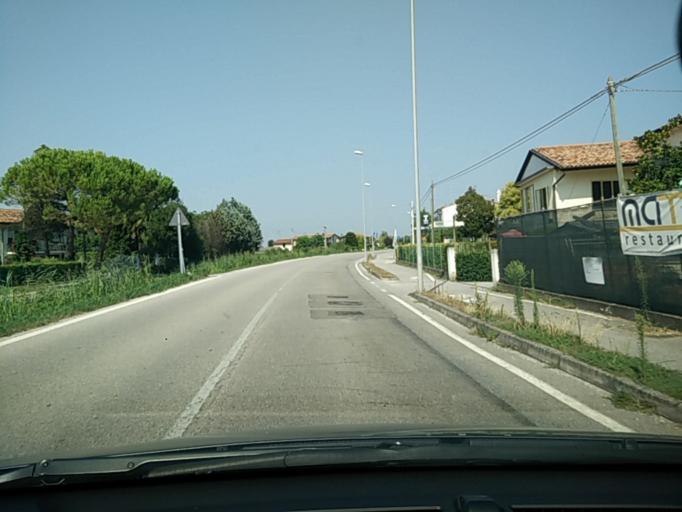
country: IT
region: Veneto
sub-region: Provincia di Venezia
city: Crepaldo
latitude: 45.6126
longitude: 12.7146
